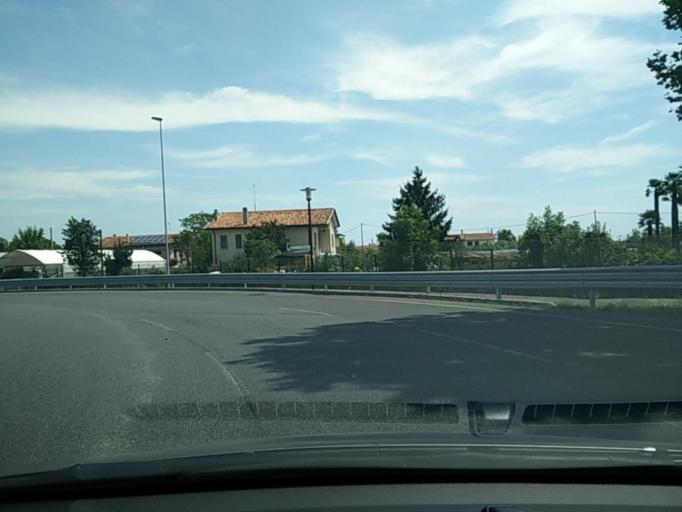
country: IT
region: Veneto
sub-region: Provincia di Venezia
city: Iesolo
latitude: 45.5480
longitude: 12.6543
